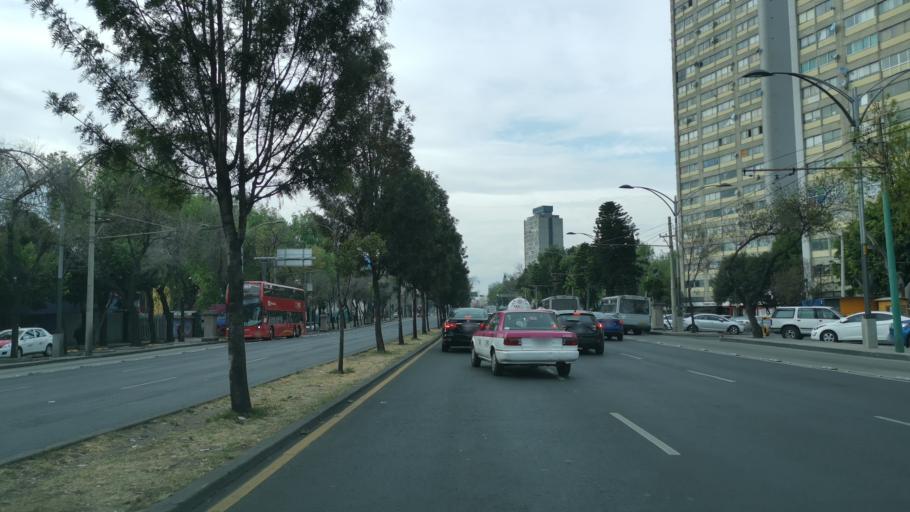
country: MX
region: Mexico City
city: Cuauhtemoc
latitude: 19.4523
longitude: -99.1315
